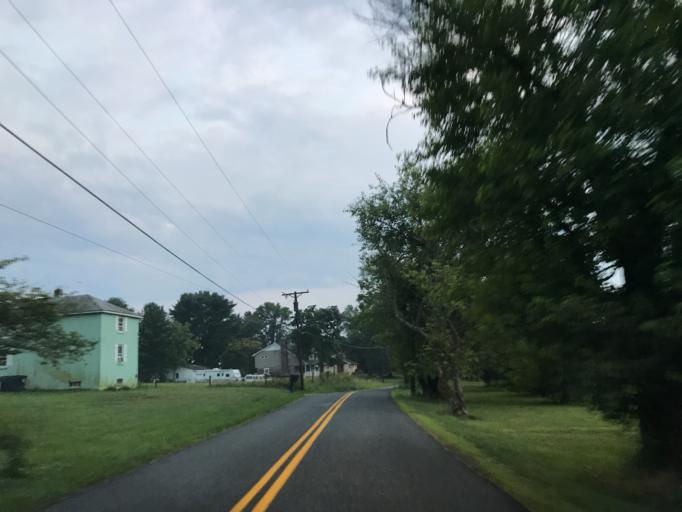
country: US
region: Maryland
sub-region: Harford County
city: Fallston
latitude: 39.5077
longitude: -76.4084
